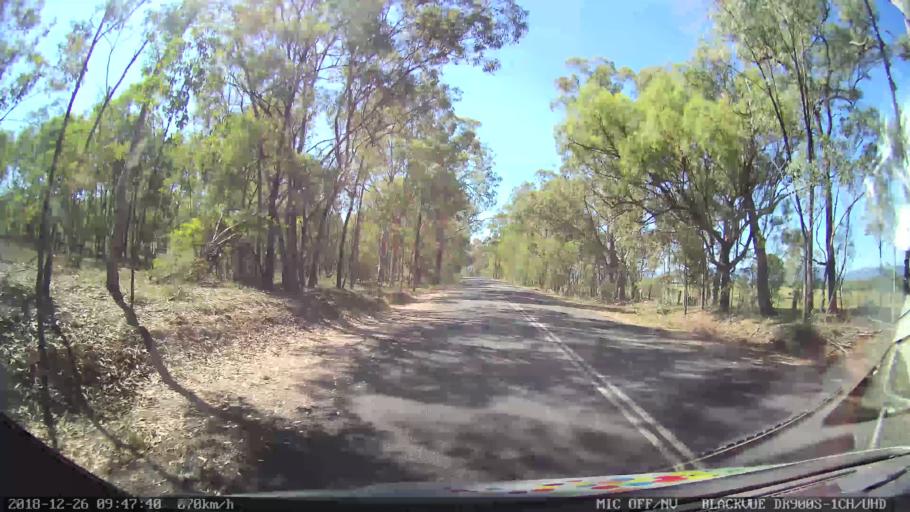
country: AU
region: New South Wales
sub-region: Mid-Western Regional
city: Kandos
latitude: -32.9813
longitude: 150.1076
